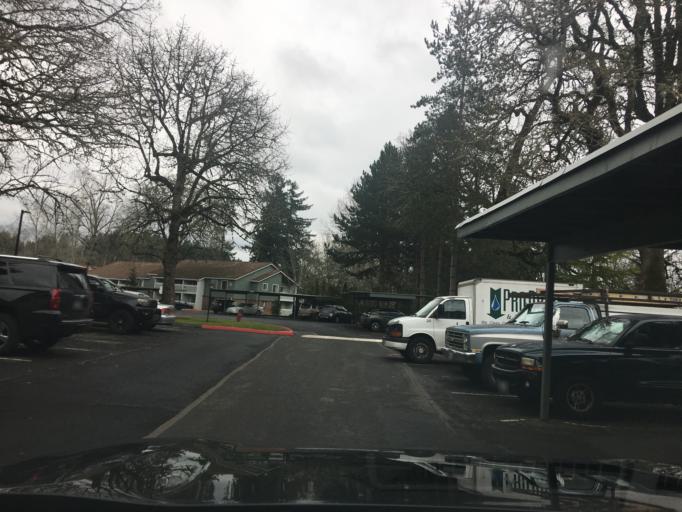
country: US
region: Oregon
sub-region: Washington County
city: Aloha
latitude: 45.4950
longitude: -122.8498
